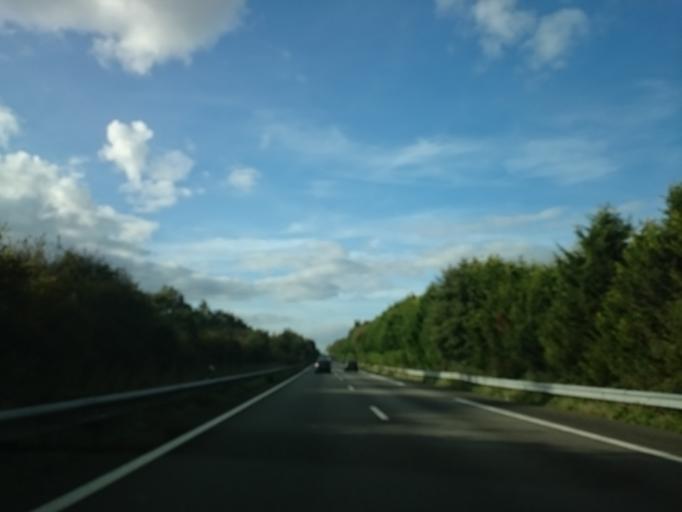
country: FR
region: Pays de la Loire
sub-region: Departement de la Loire-Atlantique
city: Jans
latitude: 47.6105
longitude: -1.6313
